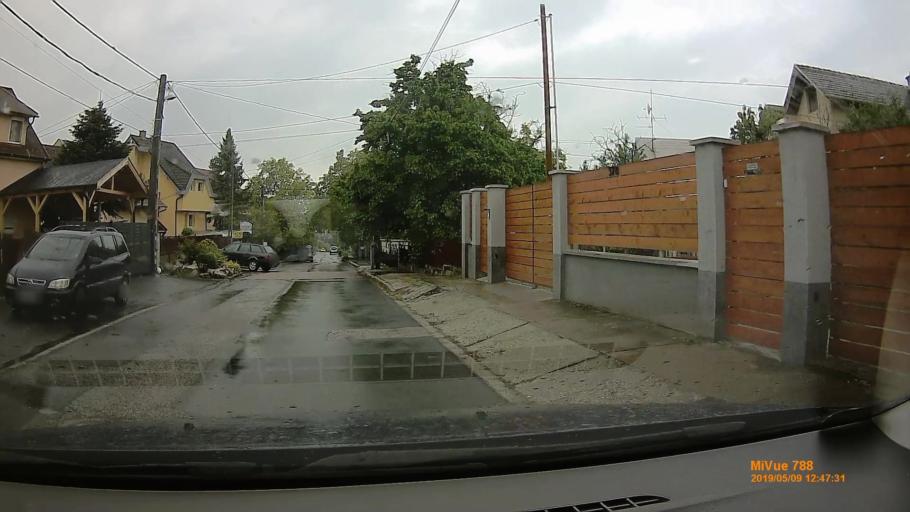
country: HU
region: Budapest
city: Budapest XVI. keruelet
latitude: 47.5367
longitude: 19.1838
